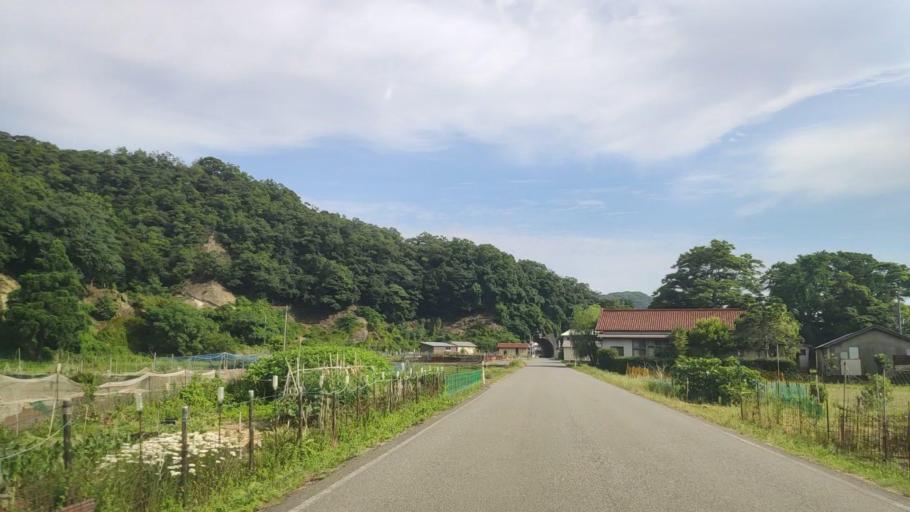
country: JP
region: Hyogo
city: Toyooka
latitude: 35.6377
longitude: 134.8363
